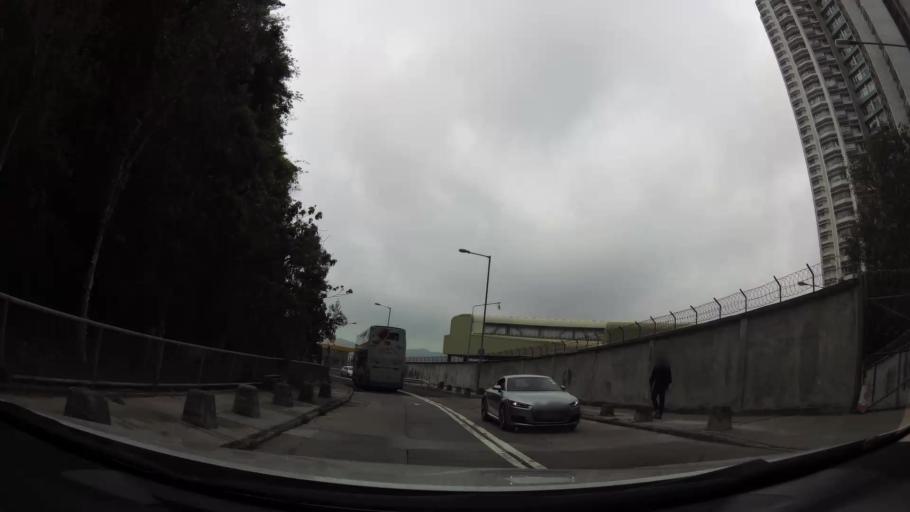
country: HK
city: Yung Shue Wan
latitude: 22.2416
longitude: 114.1487
